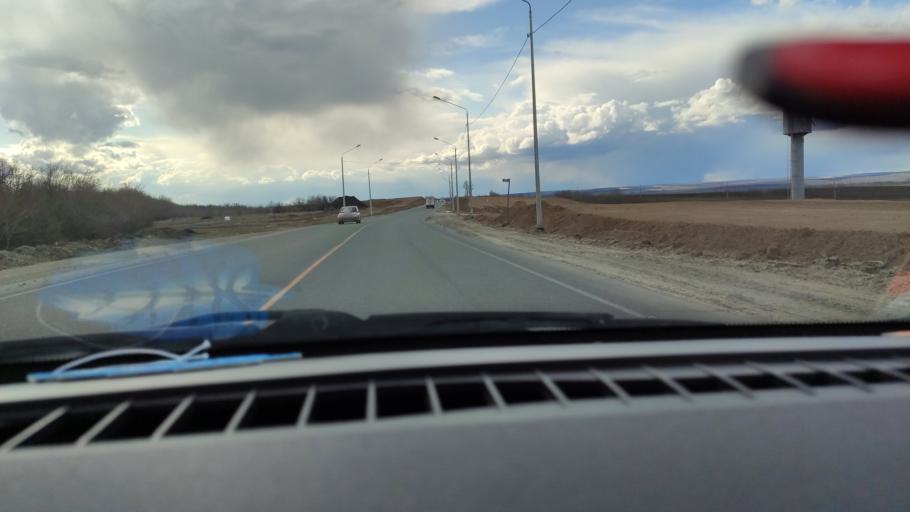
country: RU
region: Saratov
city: Sennoy
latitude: 52.1603
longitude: 47.0557
